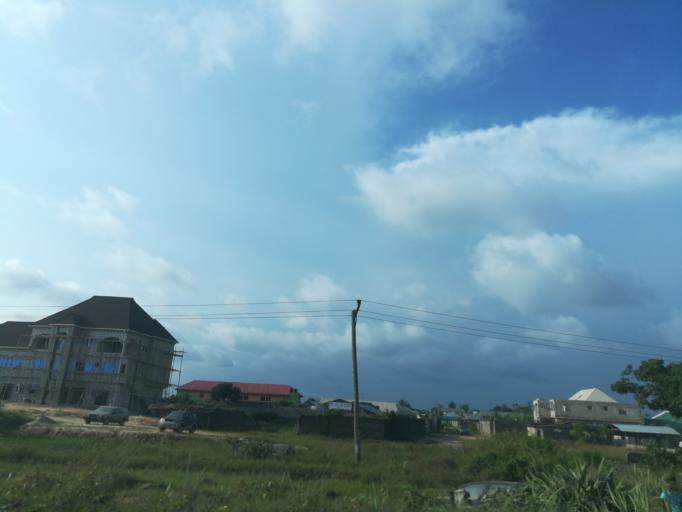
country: NG
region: Ogun
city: Ado Odo
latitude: 6.4827
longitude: 3.0367
